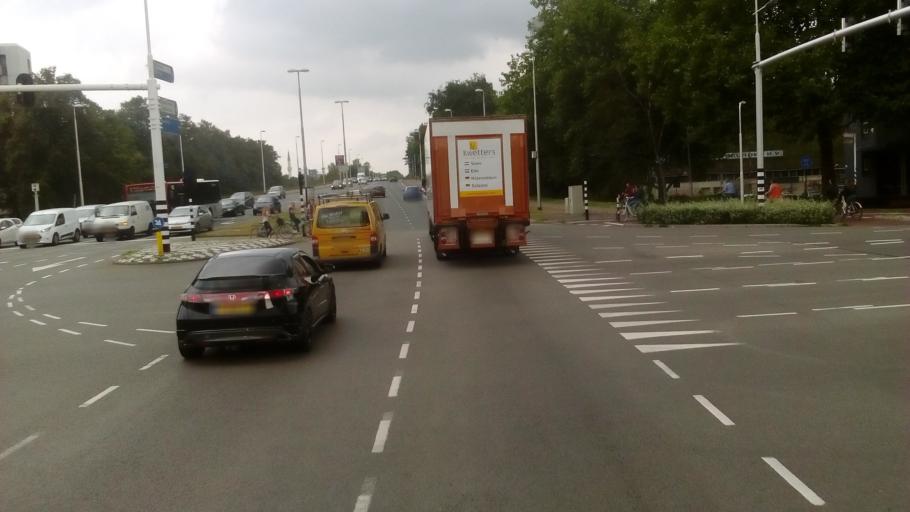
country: NL
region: North Brabant
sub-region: Gemeente Tilburg
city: Tilburg
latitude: 51.5605
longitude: 5.0650
